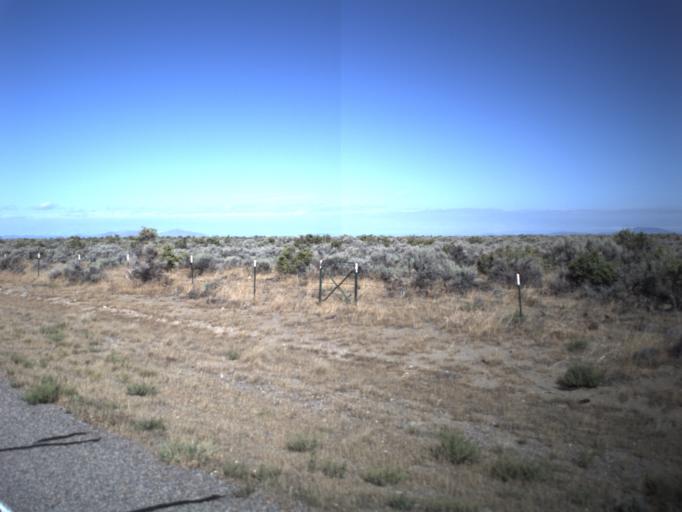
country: US
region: Utah
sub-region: Millard County
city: Delta
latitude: 39.3541
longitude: -112.4312
